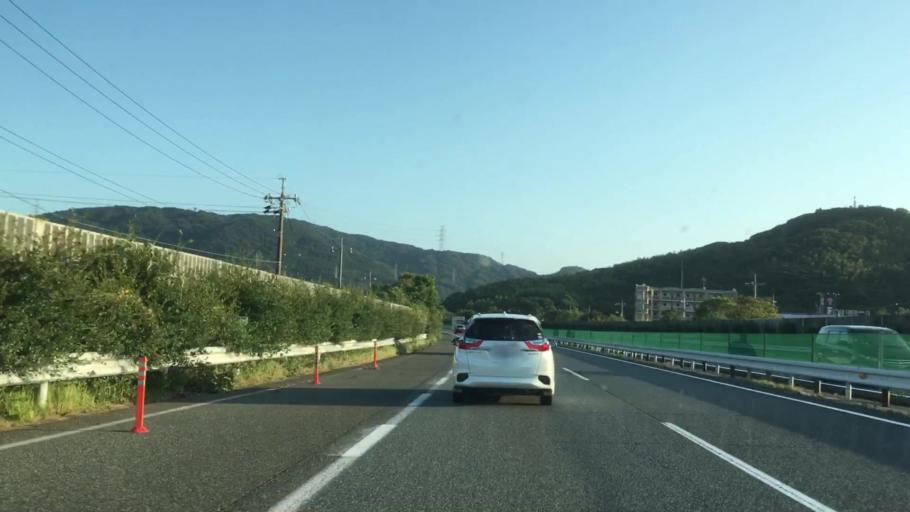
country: JP
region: Yamaguchi
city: Shimonoseki
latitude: 34.0107
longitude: 130.9555
